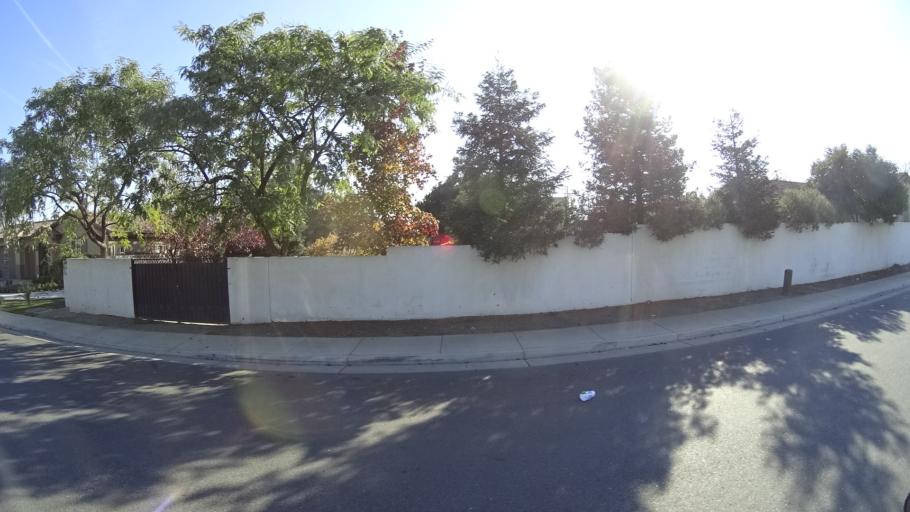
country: US
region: California
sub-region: Kern County
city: Greenfield
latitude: 35.2838
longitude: -119.0555
